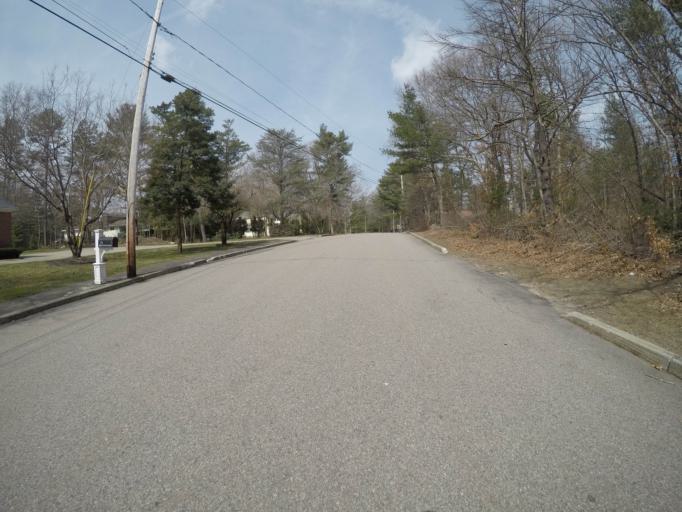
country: US
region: Massachusetts
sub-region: Bristol County
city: Easton
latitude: 42.0509
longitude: -71.1209
